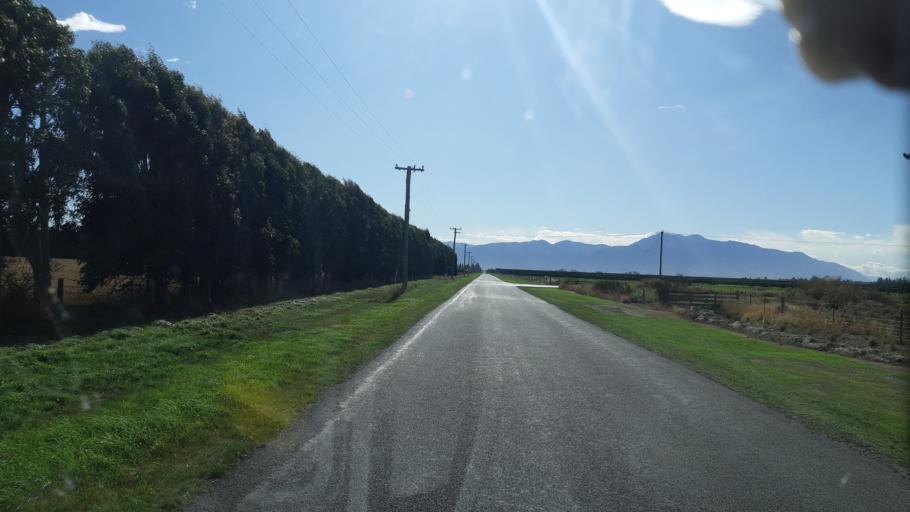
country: NZ
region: Canterbury
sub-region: Ashburton District
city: Methven
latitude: -43.6488
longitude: 171.7494
